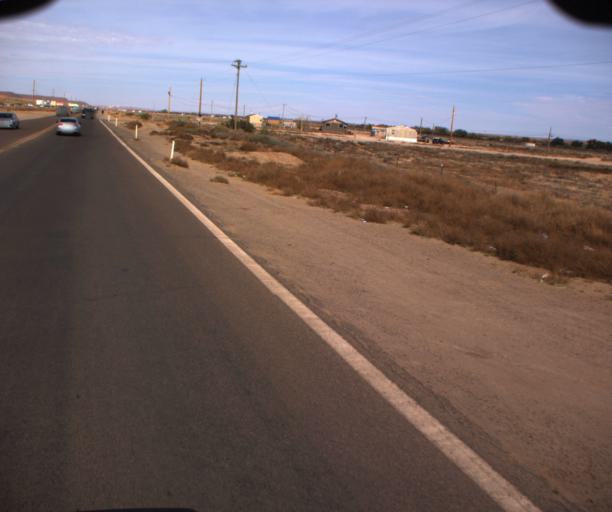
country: US
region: Arizona
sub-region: Apache County
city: Chinle
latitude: 36.1667
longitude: -109.5854
